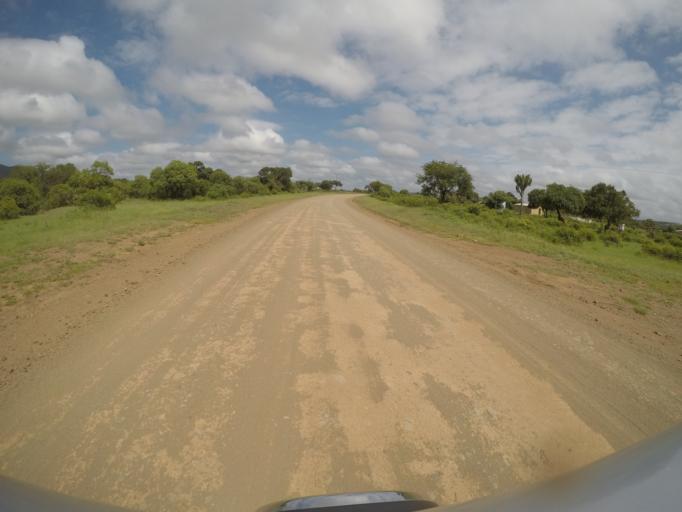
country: ZA
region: KwaZulu-Natal
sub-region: uThungulu District Municipality
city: Empangeni
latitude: -28.6212
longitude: 31.8604
